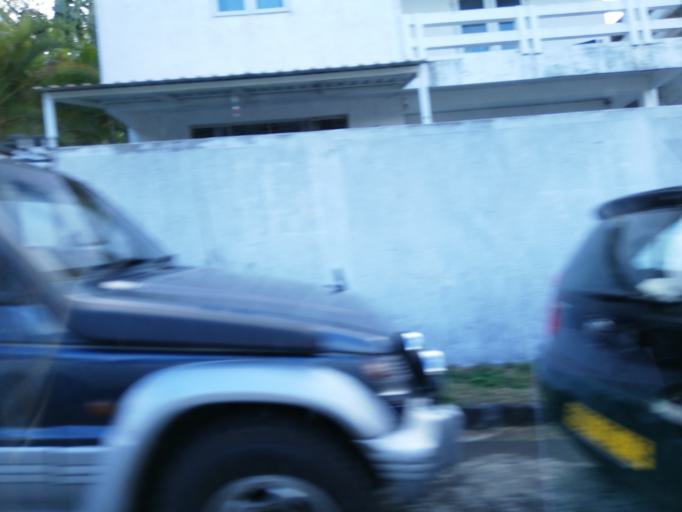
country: MU
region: Plaines Wilhems
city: Ebene
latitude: -20.2346
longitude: 57.4595
